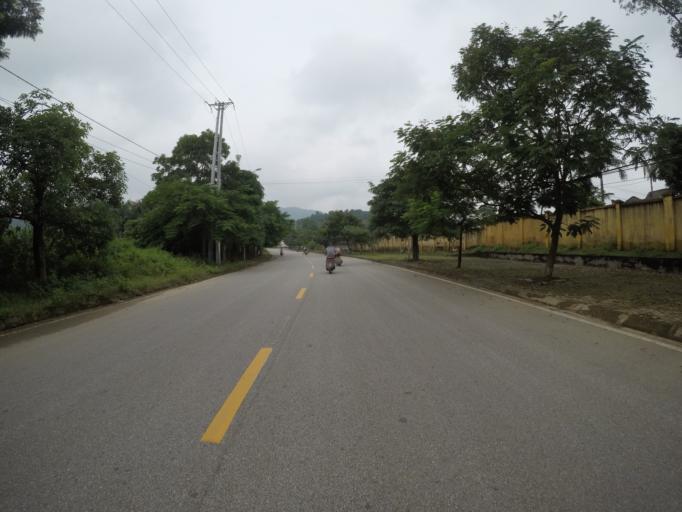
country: VN
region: Ha Noi
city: Soc Son
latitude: 21.2831
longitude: 105.8413
